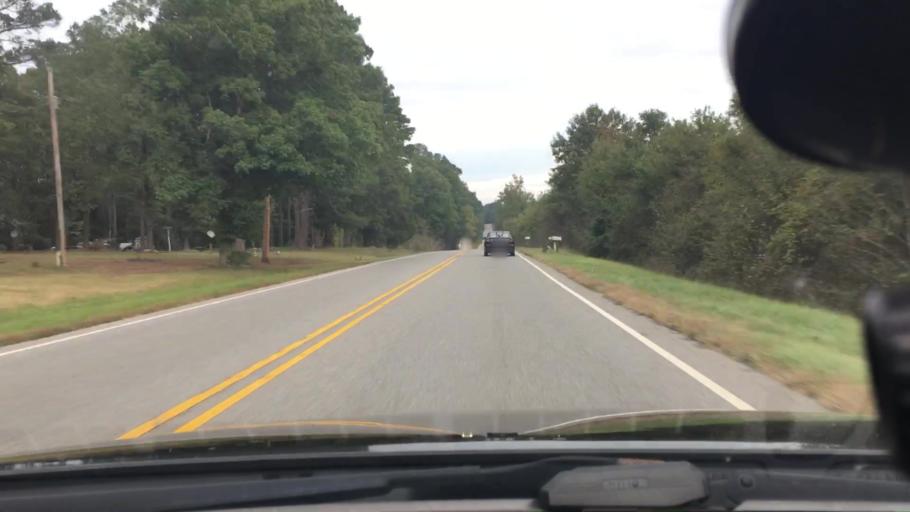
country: US
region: North Carolina
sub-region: Montgomery County
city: Biscoe
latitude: 35.3604
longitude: -79.7085
